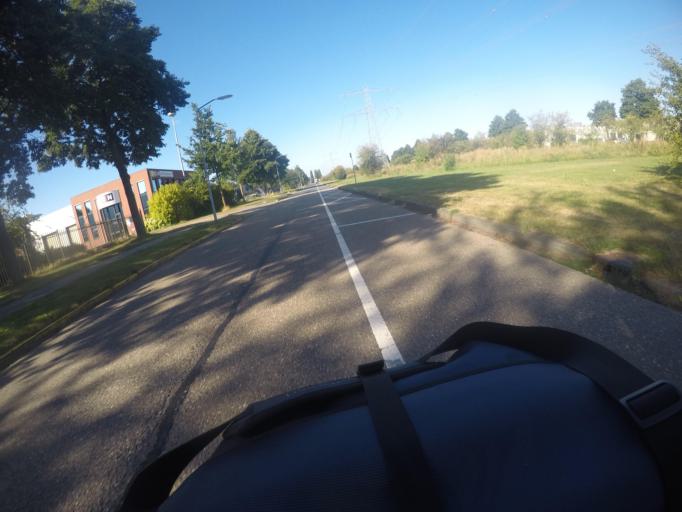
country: NL
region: Flevoland
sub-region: Gemeente Almere
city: Almere Stad
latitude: 52.3512
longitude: 5.1901
